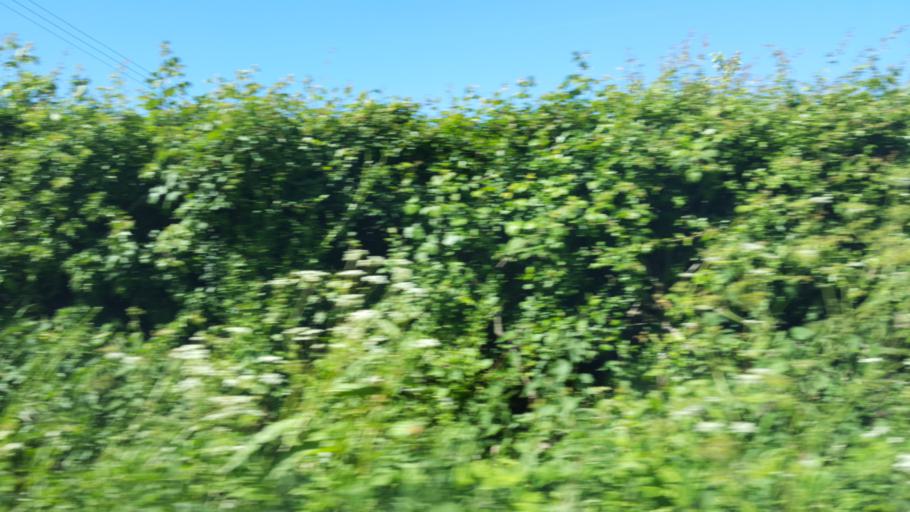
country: GB
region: England
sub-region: South Gloucestershire
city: Alveston
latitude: 51.5554
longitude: -2.5267
